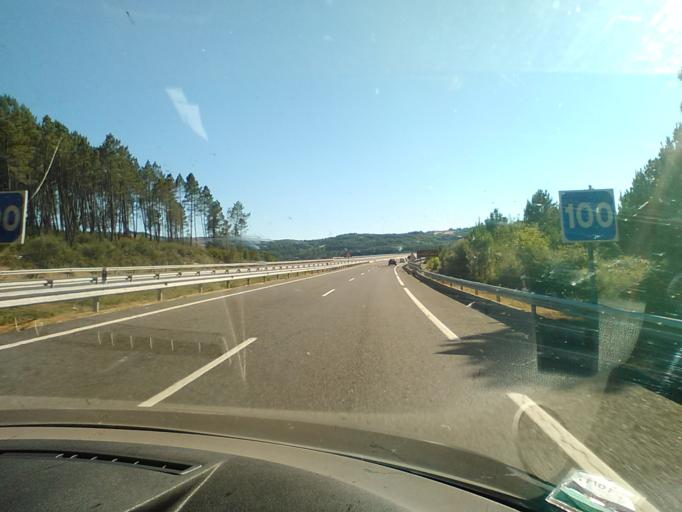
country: ES
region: Galicia
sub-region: Provincia de Ourense
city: Rios
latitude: 41.9955
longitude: -7.2332
